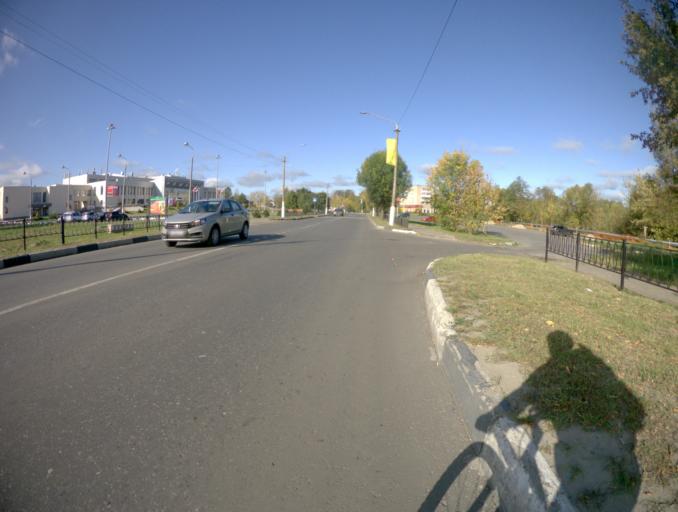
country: RU
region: Moskovskaya
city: Roshal'
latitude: 55.6635
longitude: 39.8649
